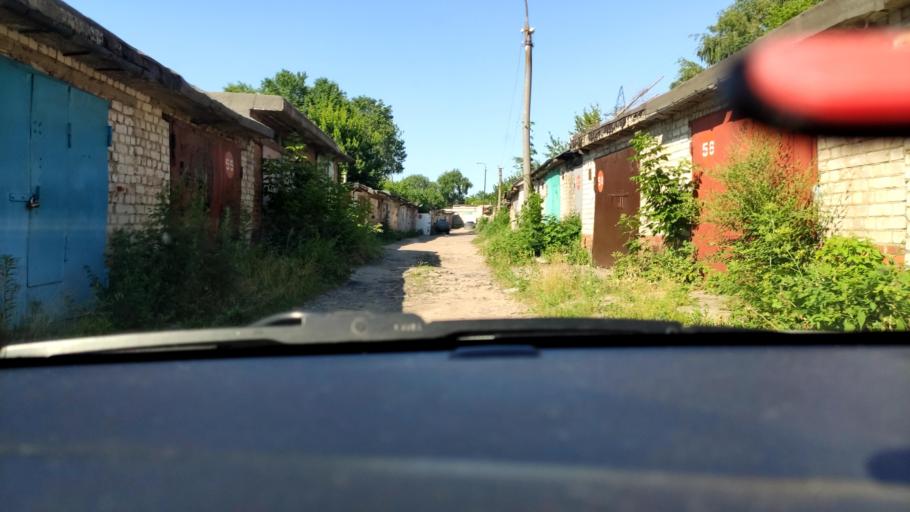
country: RU
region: Voronezj
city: Voronezh
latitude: 51.6822
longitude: 39.1348
